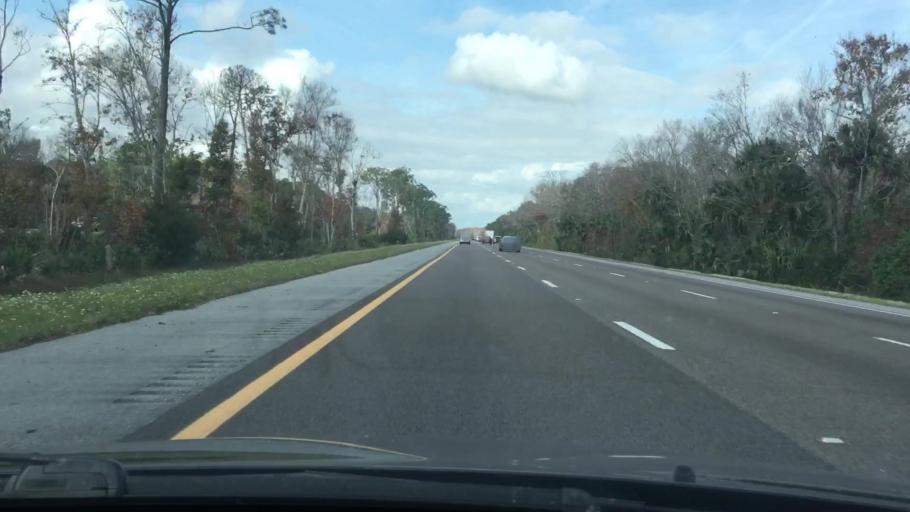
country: US
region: Florida
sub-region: Volusia County
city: Edgewater
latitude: 28.9124
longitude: -80.9347
